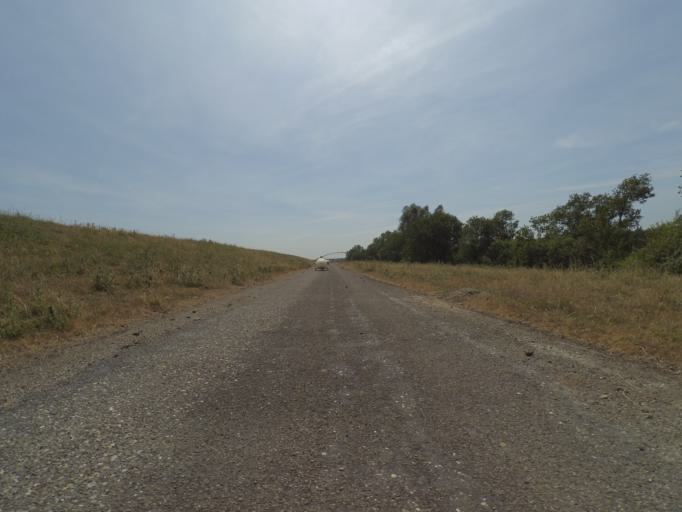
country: NL
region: North Brabant
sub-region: Gemeente Steenbergen
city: Nieuw-Vossemeer
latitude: 51.5909
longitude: 4.1964
